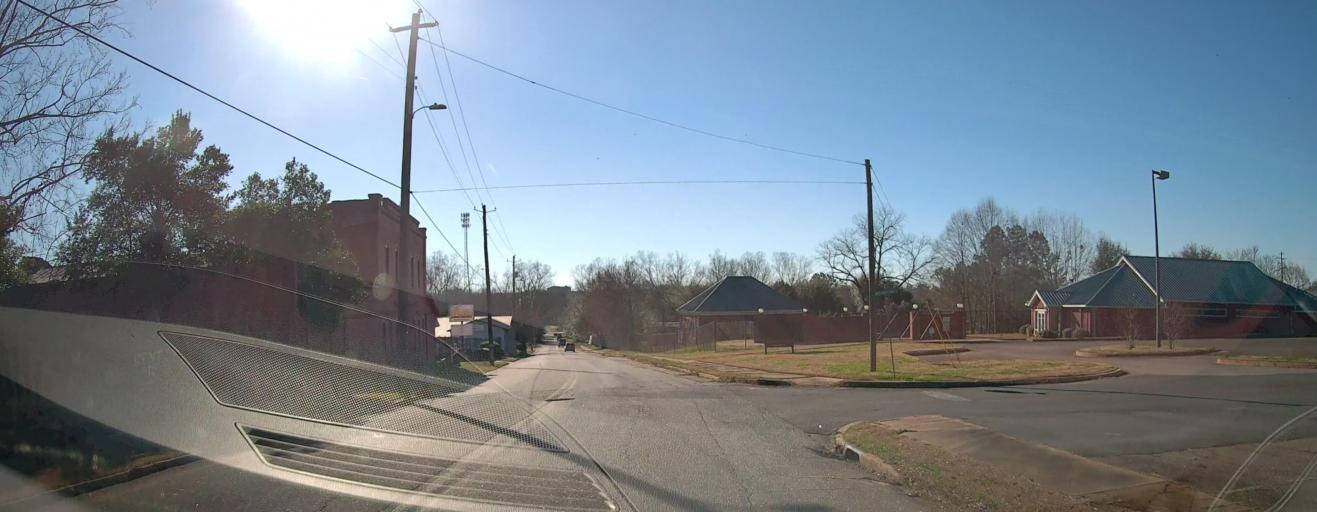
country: US
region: Georgia
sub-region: Sumter County
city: Americus
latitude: 32.0702
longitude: -84.2398
